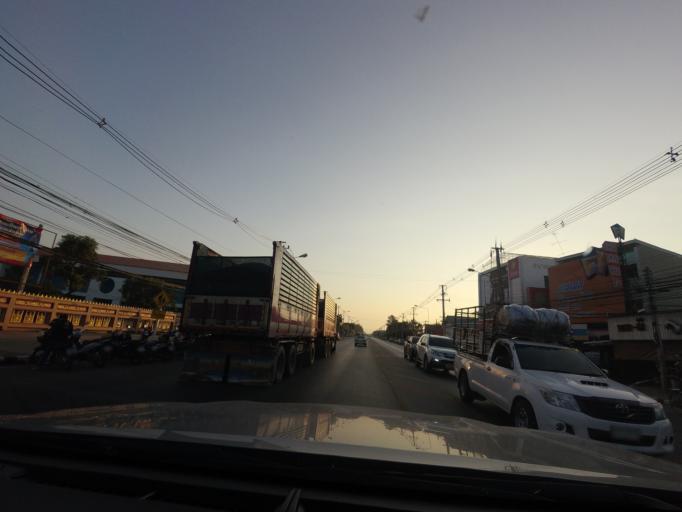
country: TH
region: Sukhothai
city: Si Samrong
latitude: 17.1655
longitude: 99.8637
